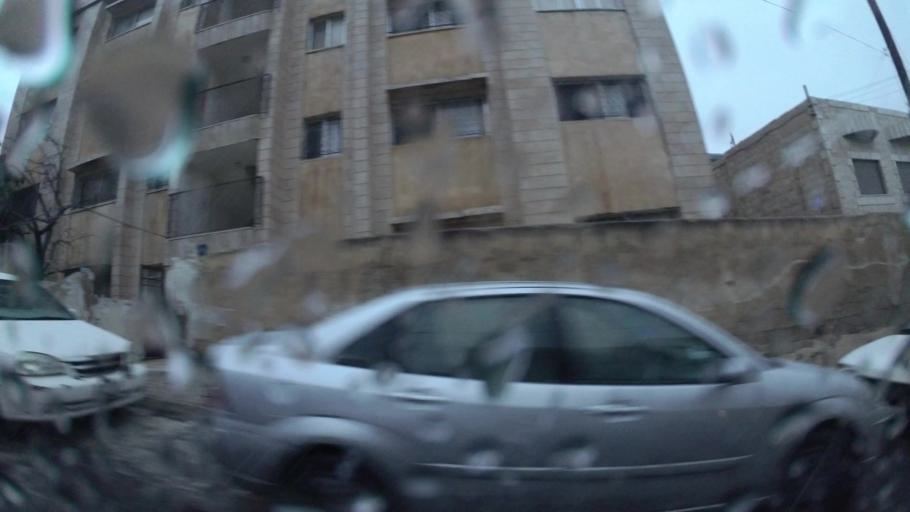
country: JO
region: Amman
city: Al Jubayhah
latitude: 32.0265
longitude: 35.8451
